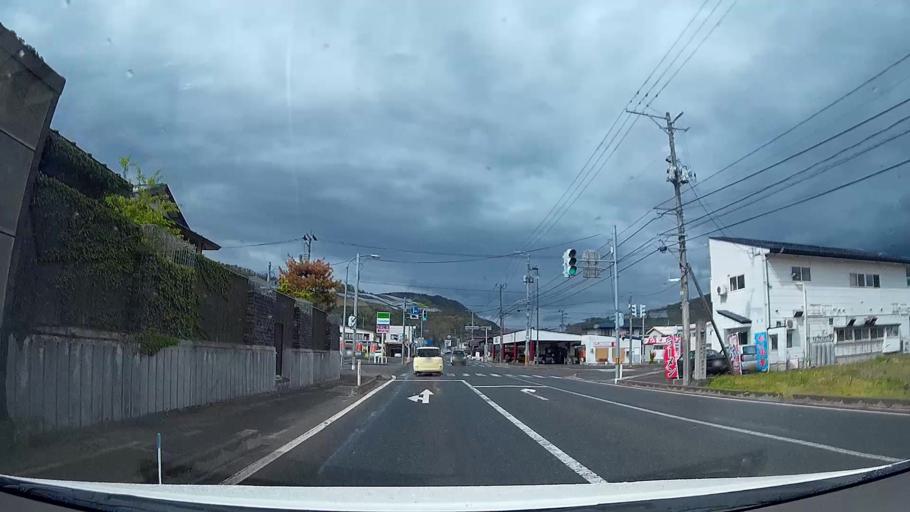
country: JP
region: Yamagata
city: Takahata
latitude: 38.0488
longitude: 140.1708
